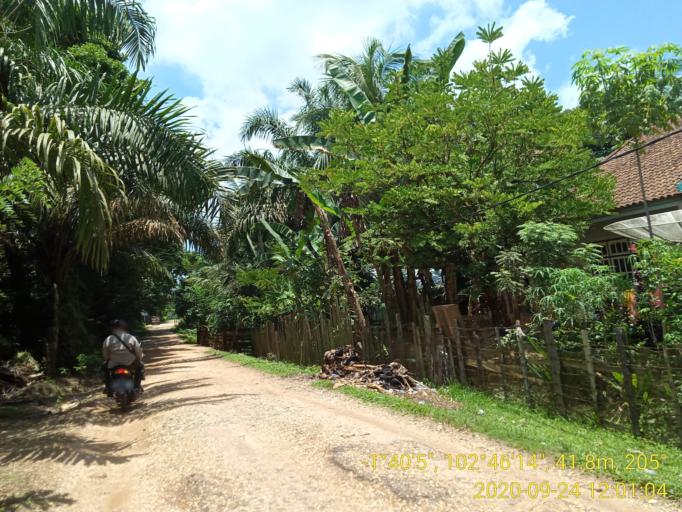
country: ID
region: Jambi
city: Sungaibengkal
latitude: -1.6683
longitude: 102.7706
